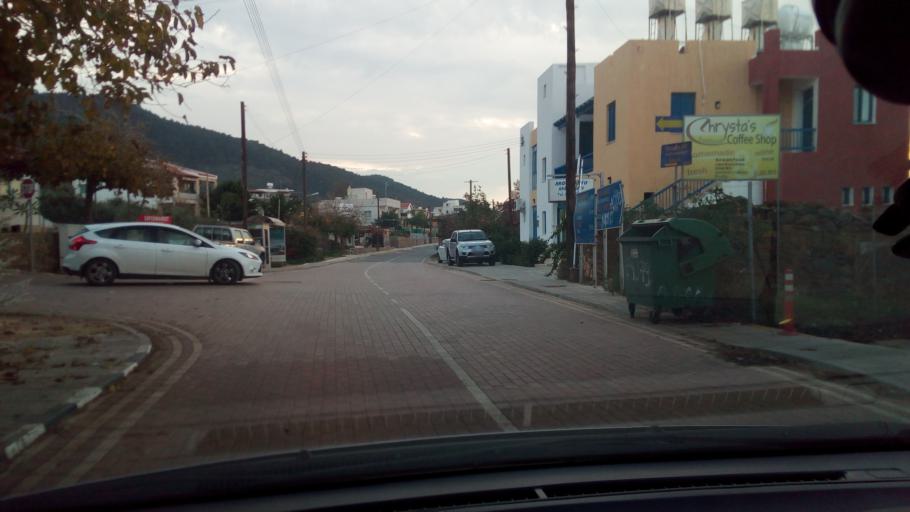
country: CY
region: Lefkosia
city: Kato Pyrgos
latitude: 35.1603
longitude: 32.5449
